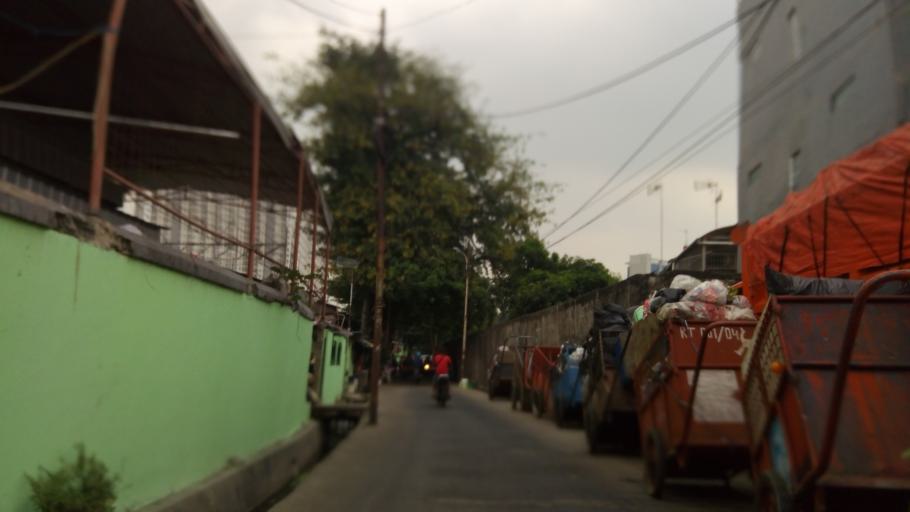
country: ID
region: Jakarta Raya
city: Jakarta
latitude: -6.1519
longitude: 106.8390
